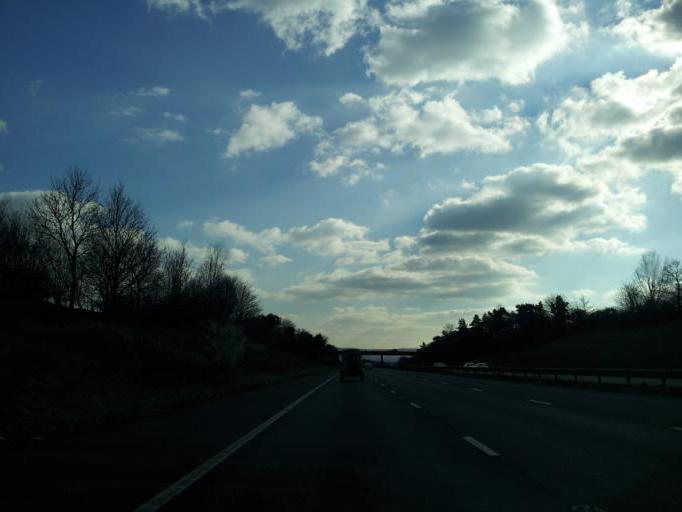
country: GB
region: England
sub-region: Somerset
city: Creech Saint Michael
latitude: 51.0500
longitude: -3.0274
